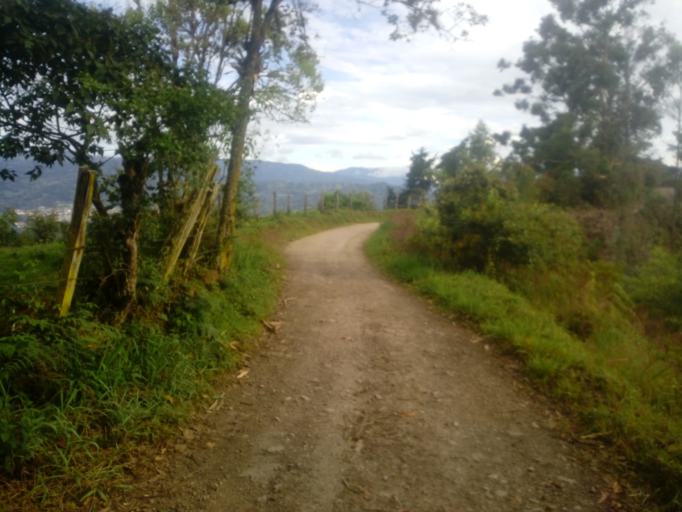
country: CO
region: Cundinamarca
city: Tenza
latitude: 5.1027
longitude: -73.4181
